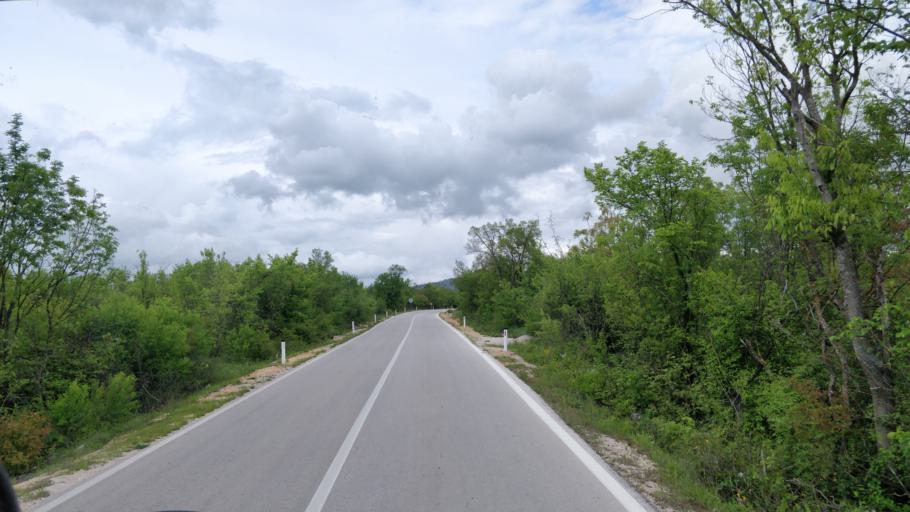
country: BA
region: Federation of Bosnia and Herzegovina
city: Ljubuski
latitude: 43.1766
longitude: 17.5054
